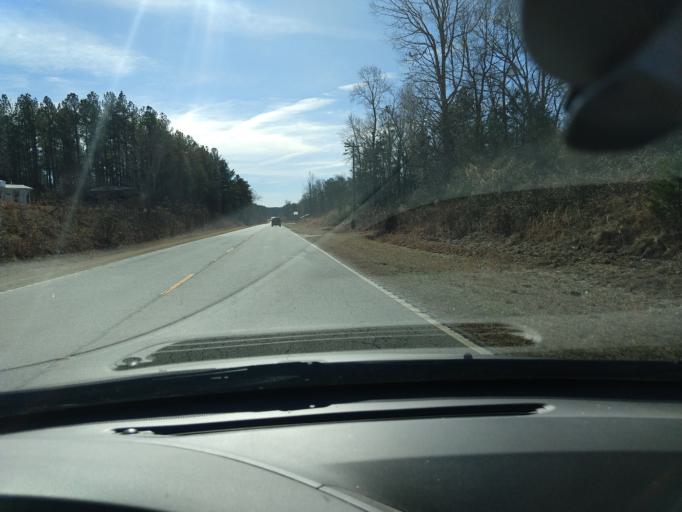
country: US
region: South Carolina
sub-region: Oconee County
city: Westminster
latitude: 34.6373
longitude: -83.1350
